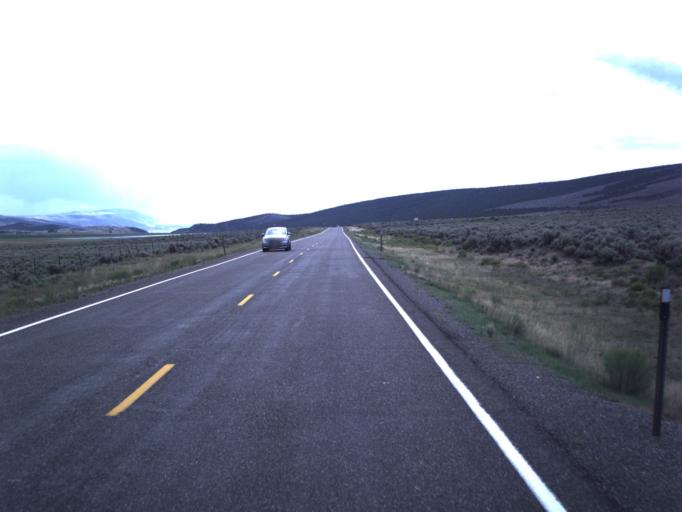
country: US
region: Utah
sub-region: Sevier County
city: Monroe
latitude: 38.6252
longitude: -111.8347
